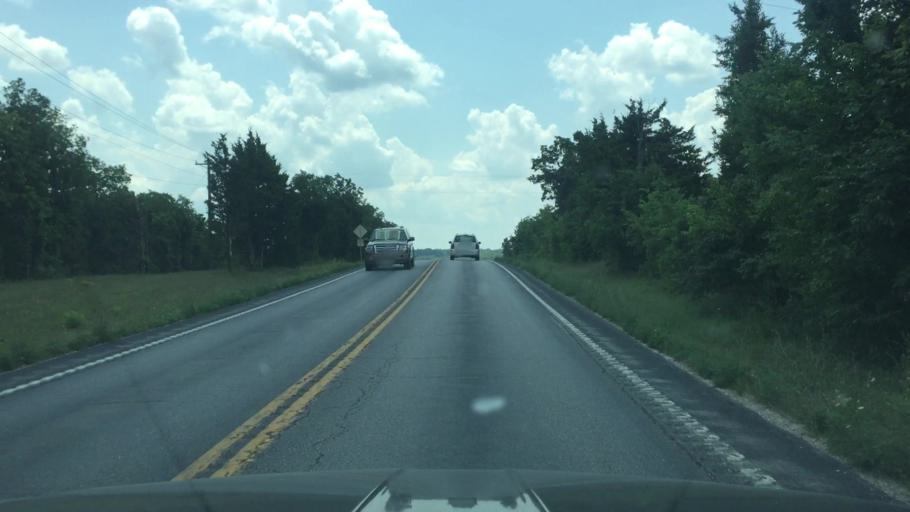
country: US
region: Missouri
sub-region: Miller County
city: Tuscumbia
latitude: 38.0915
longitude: -92.4989
